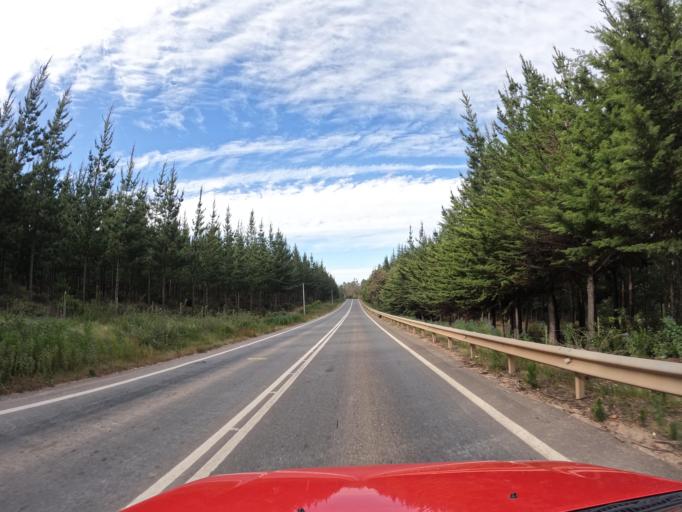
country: CL
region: O'Higgins
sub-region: Provincia de Colchagua
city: Santa Cruz
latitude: -34.3180
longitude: -71.8647
